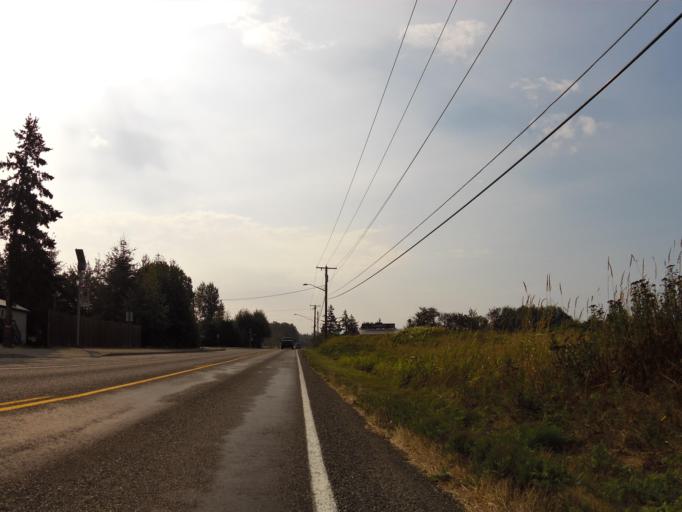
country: US
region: Washington
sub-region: Whatcom County
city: Marietta
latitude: 48.8062
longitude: -122.6279
